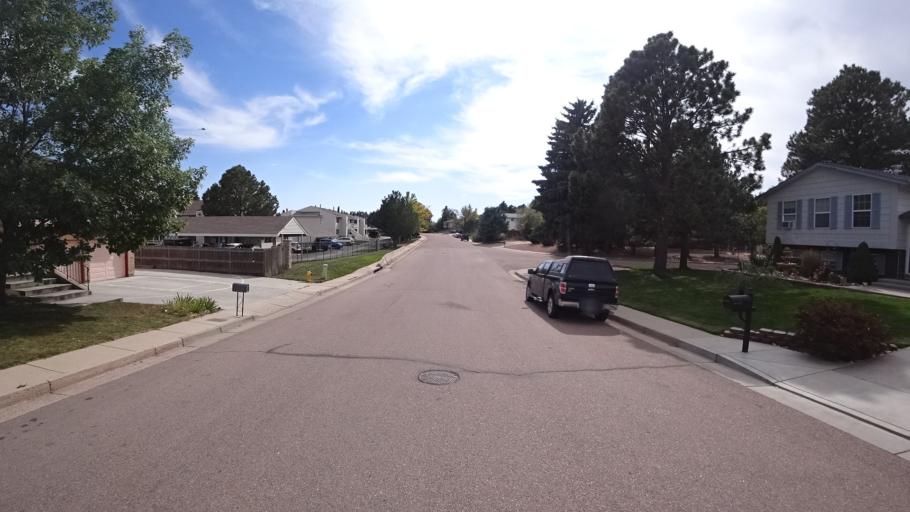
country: US
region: Colorado
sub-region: El Paso County
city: Colorado Springs
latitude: 38.9026
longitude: -104.7797
